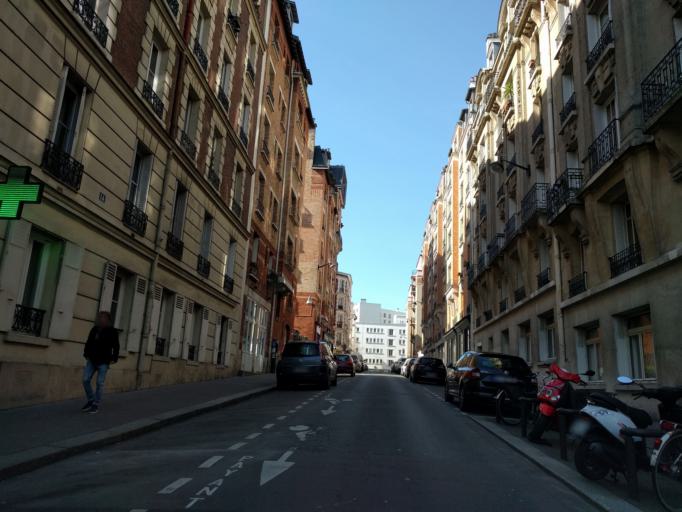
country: FR
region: Ile-de-France
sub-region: Departement du Val-de-Marne
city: Saint-Mande
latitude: 48.8382
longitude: 2.3991
